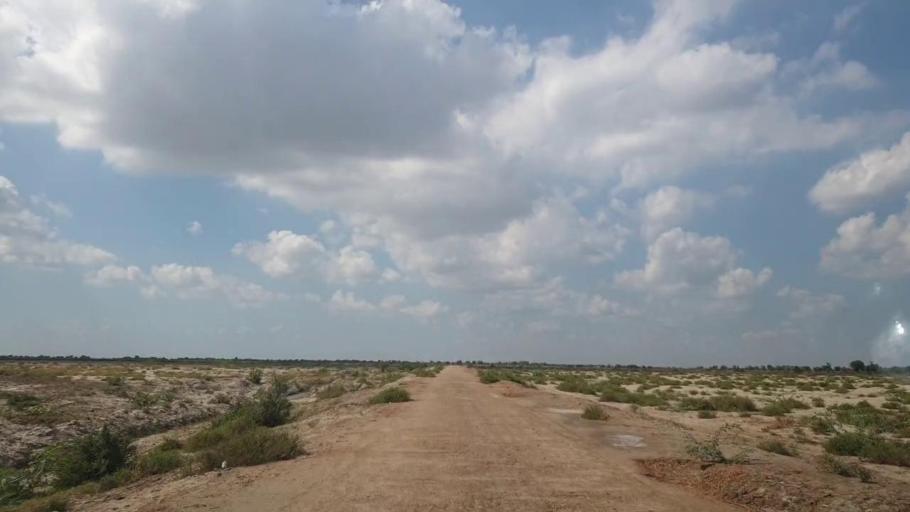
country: PK
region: Sindh
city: Pithoro
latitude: 25.5925
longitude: 69.3590
